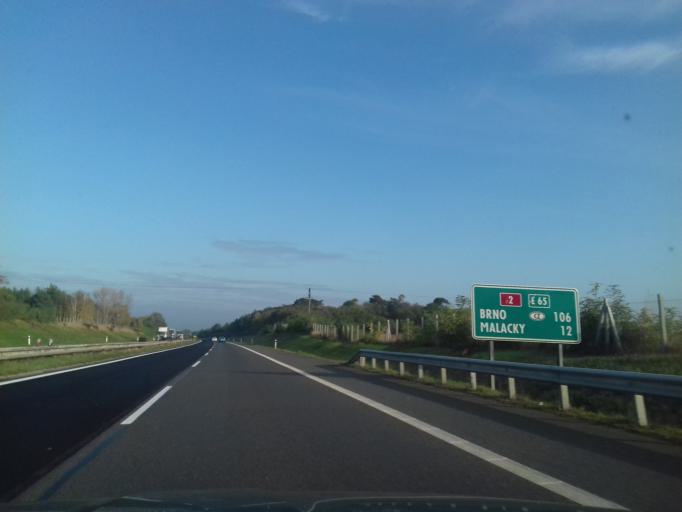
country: SK
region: Bratislavsky
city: Stupava
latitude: 48.3320
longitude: 17.0243
